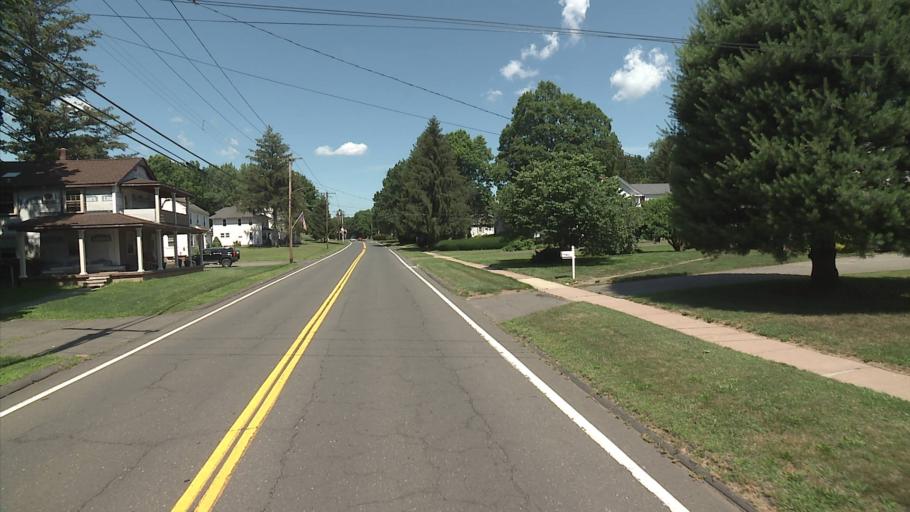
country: US
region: Connecticut
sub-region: Middlesex County
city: Cromwell
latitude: 41.5974
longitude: -72.6497
